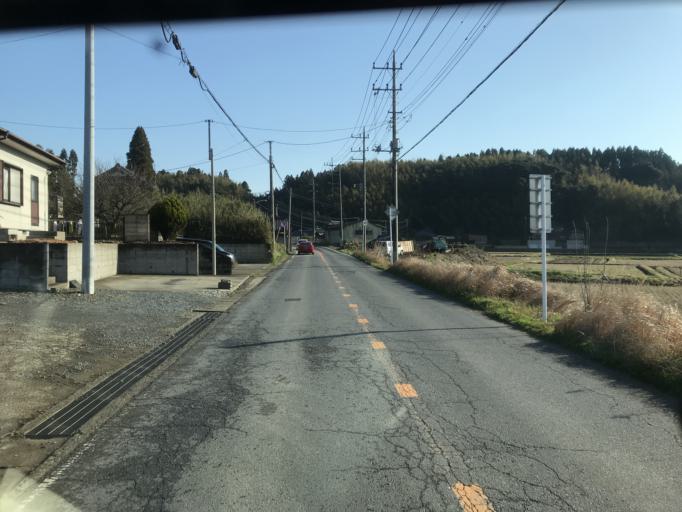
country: JP
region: Chiba
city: Sawara
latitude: 35.8764
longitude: 140.4952
